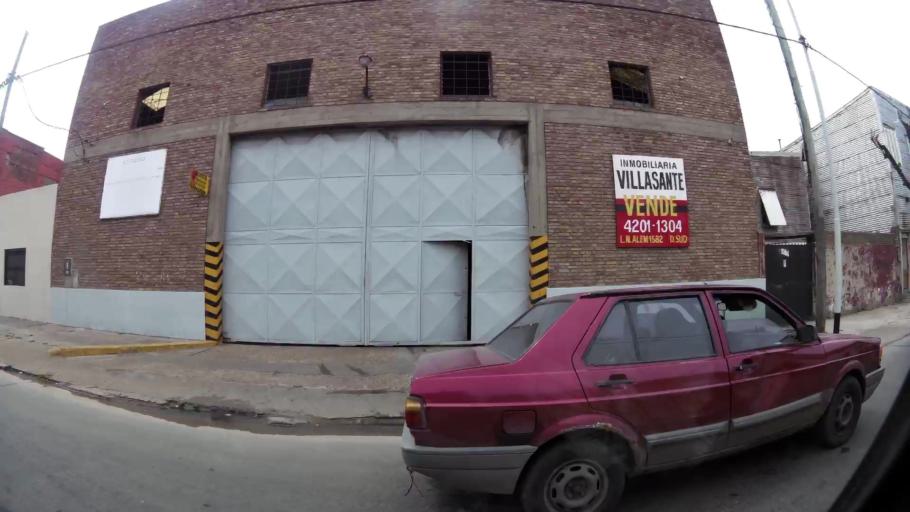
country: AR
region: Buenos Aires
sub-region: Partido de Avellaneda
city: Avellaneda
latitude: -34.6524
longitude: -58.3478
